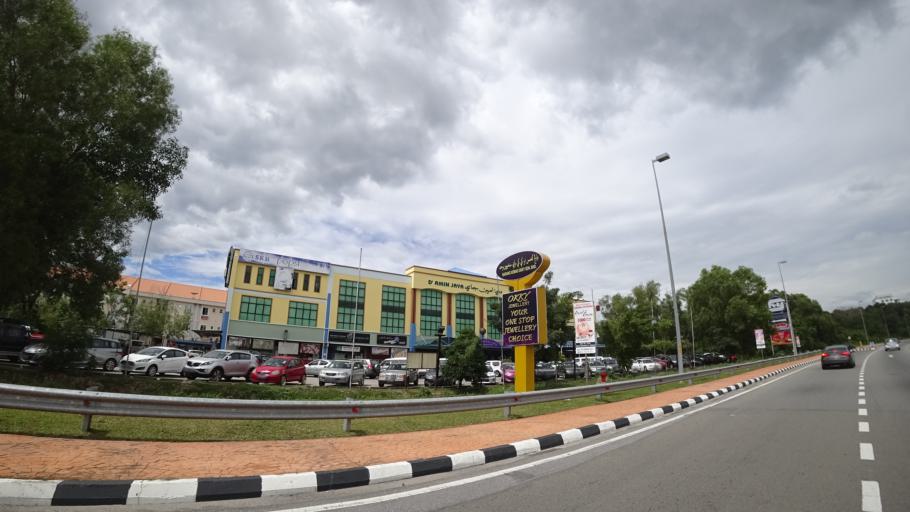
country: BN
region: Brunei and Muara
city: Bandar Seri Begawan
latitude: 4.9010
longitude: 114.9209
